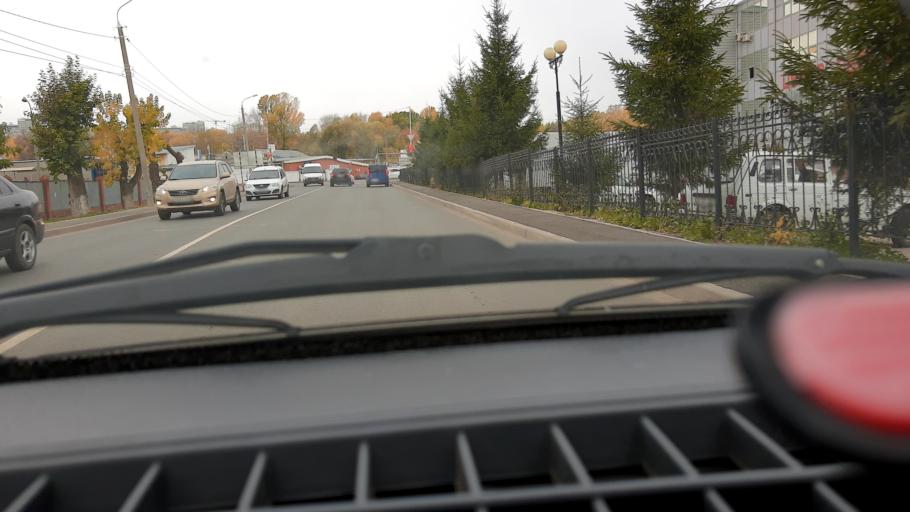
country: RU
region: Bashkortostan
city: Ufa
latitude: 54.7879
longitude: 56.0589
